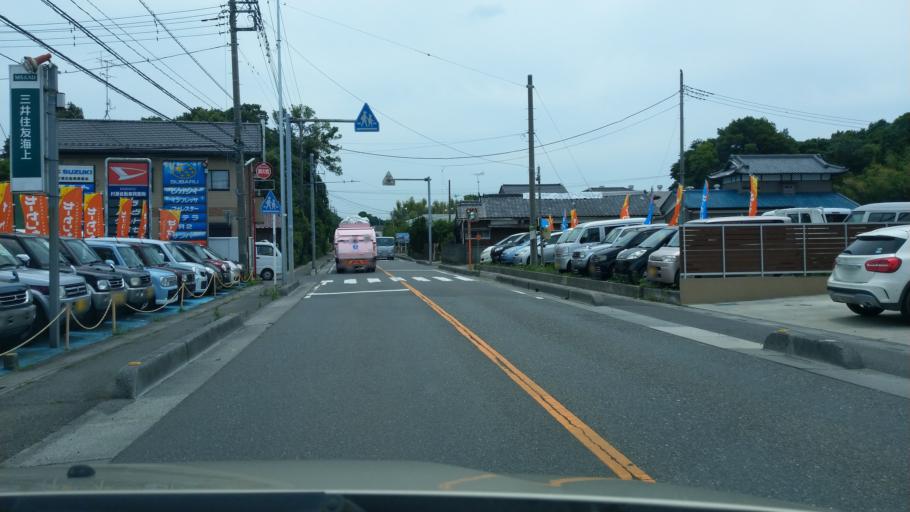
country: JP
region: Saitama
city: Saitama
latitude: 35.9117
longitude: 139.6942
